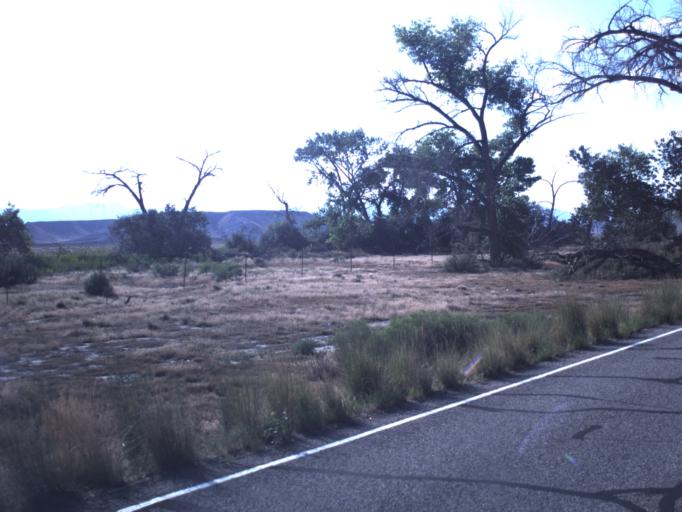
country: US
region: Utah
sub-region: Emery County
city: Huntington
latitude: 39.4187
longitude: -110.8576
